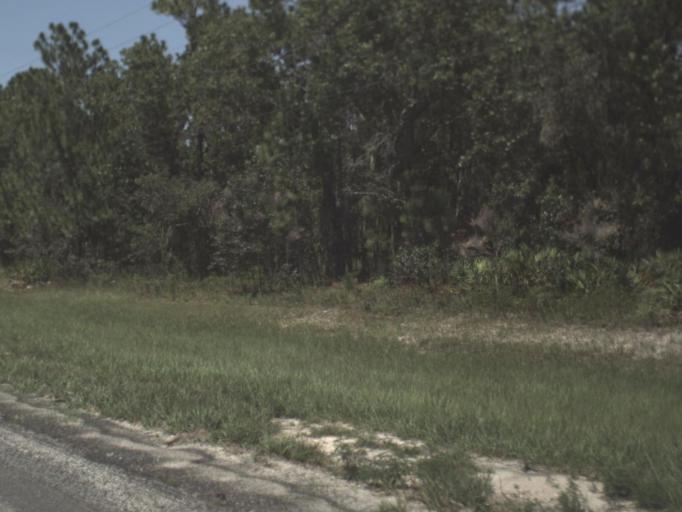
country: US
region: Florida
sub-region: Citrus County
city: Sugarmill Woods
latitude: 28.6641
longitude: -82.5521
